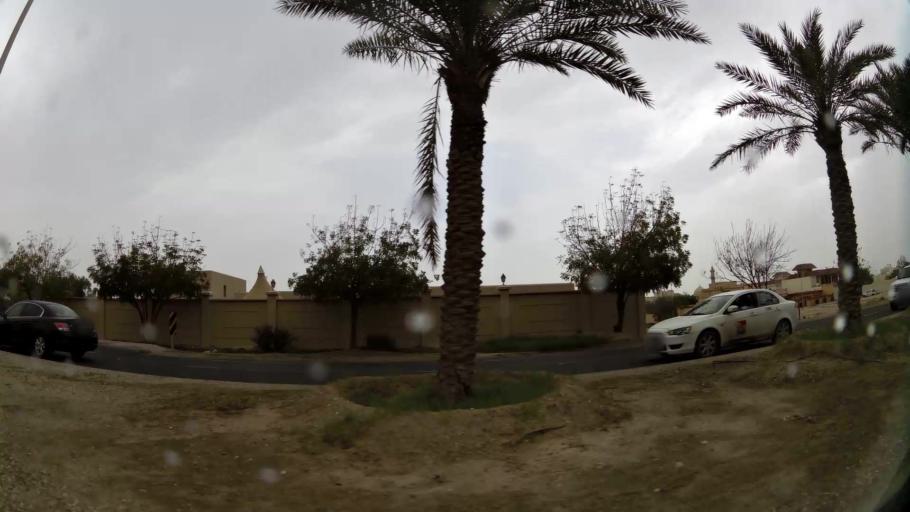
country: BH
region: Northern
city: Ar Rifa'
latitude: 26.1406
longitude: 50.5565
